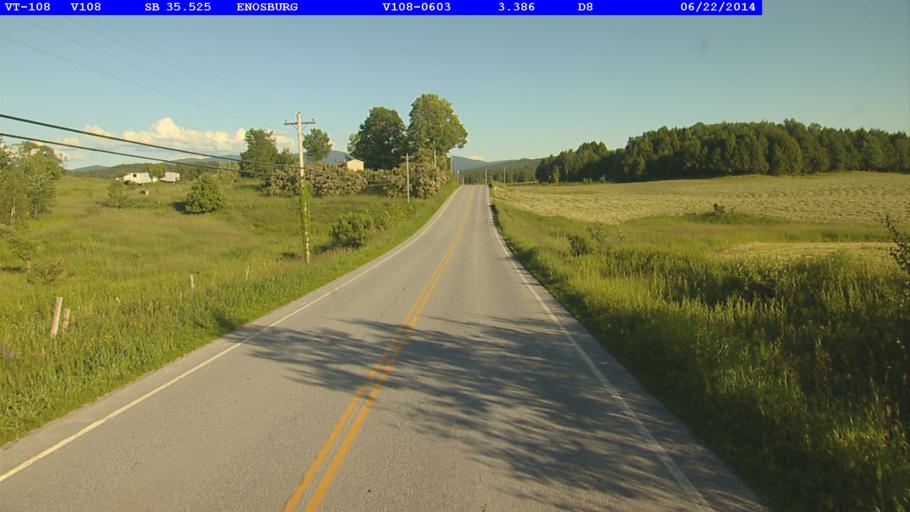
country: US
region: Vermont
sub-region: Franklin County
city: Enosburg Falls
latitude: 44.8846
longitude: -72.8010
